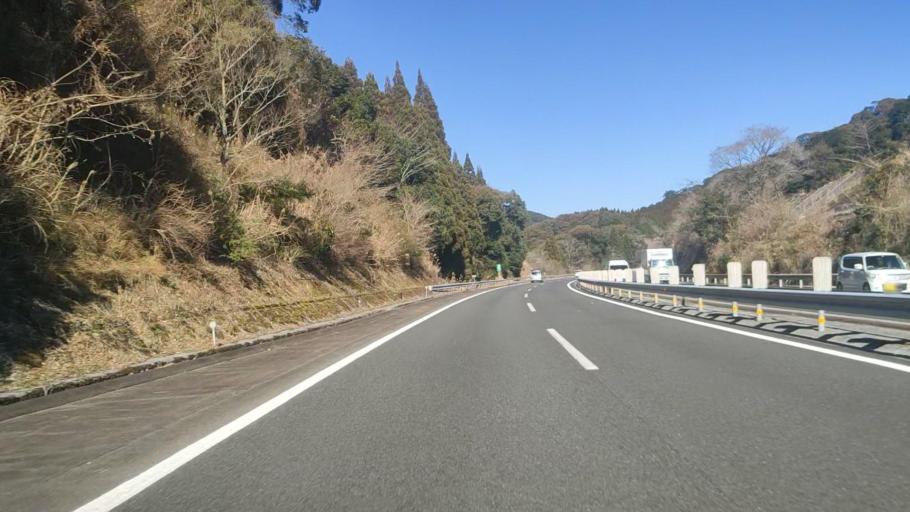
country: JP
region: Miyazaki
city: Miyakonojo
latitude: 31.8174
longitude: 131.2163
